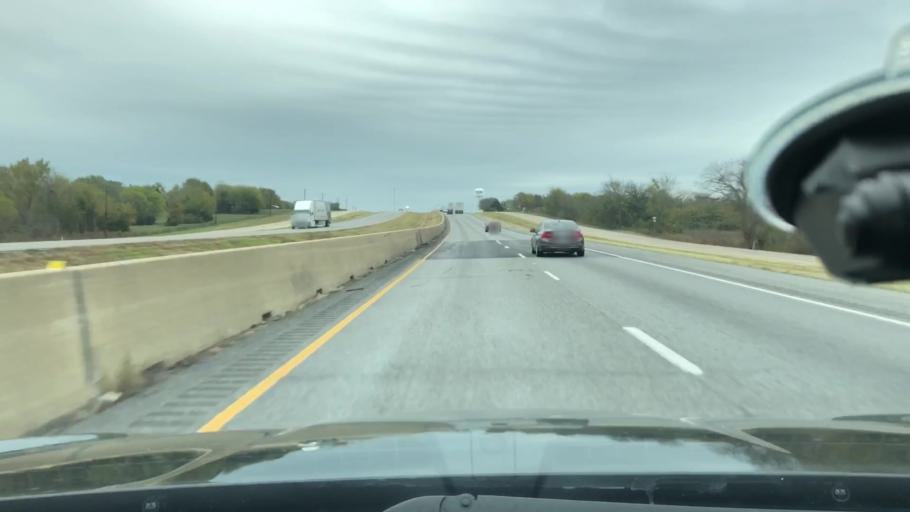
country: US
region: Texas
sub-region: Hunt County
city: Commerce
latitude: 33.1303
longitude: -95.8961
